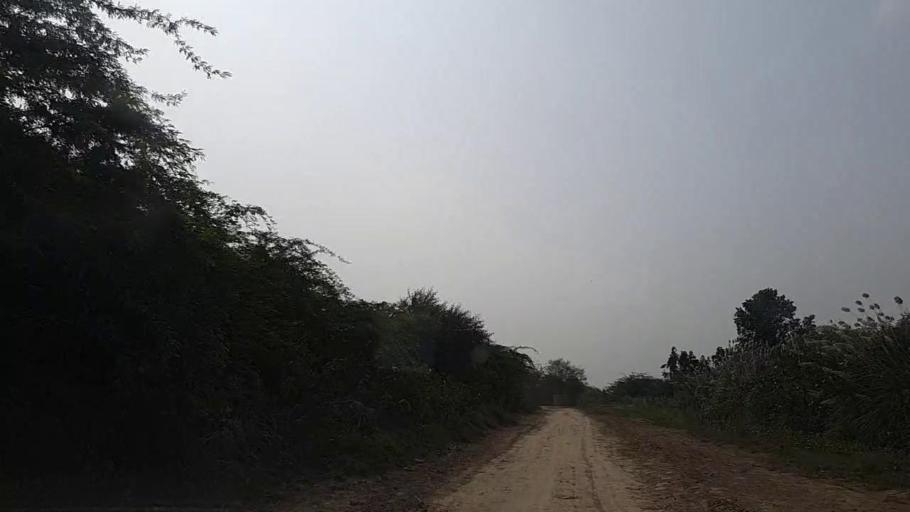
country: PK
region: Sindh
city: Mirpur Sakro
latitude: 24.6500
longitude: 67.7672
